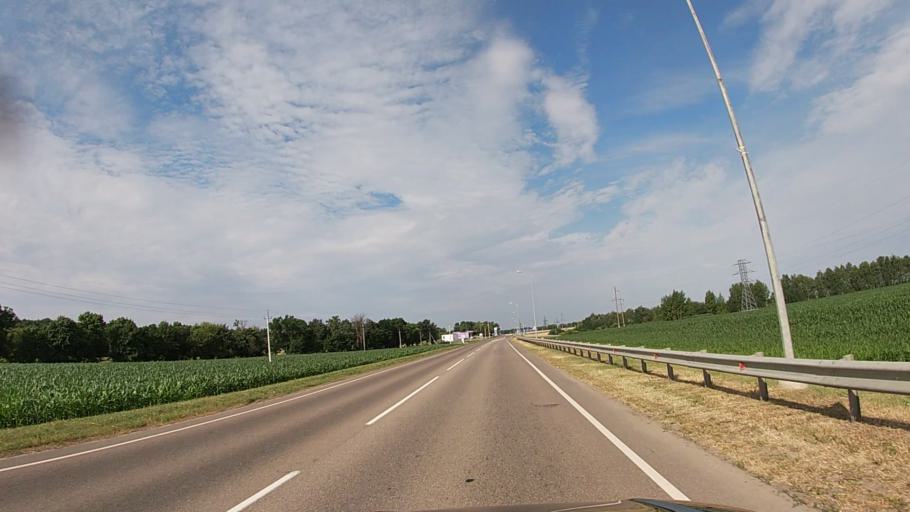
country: RU
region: Belgorod
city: Proletarskiy
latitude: 50.7980
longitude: 35.7184
